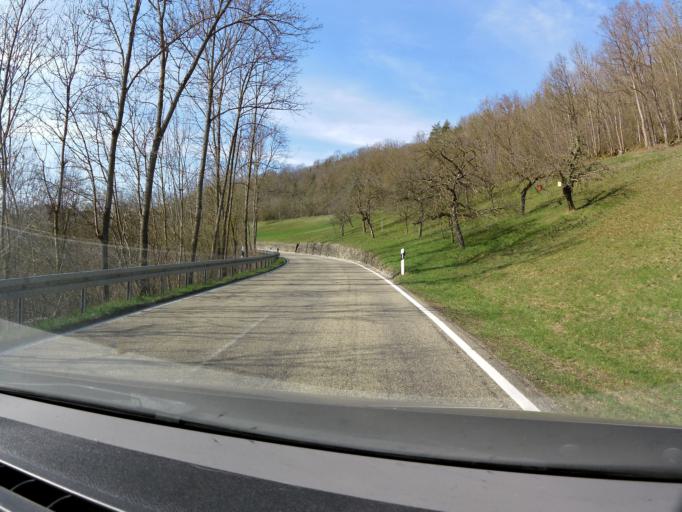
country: DE
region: Bavaria
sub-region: Regierungsbezirk Mittelfranken
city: Rothenburg ob der Tauber
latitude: 49.3973
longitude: 10.1668
